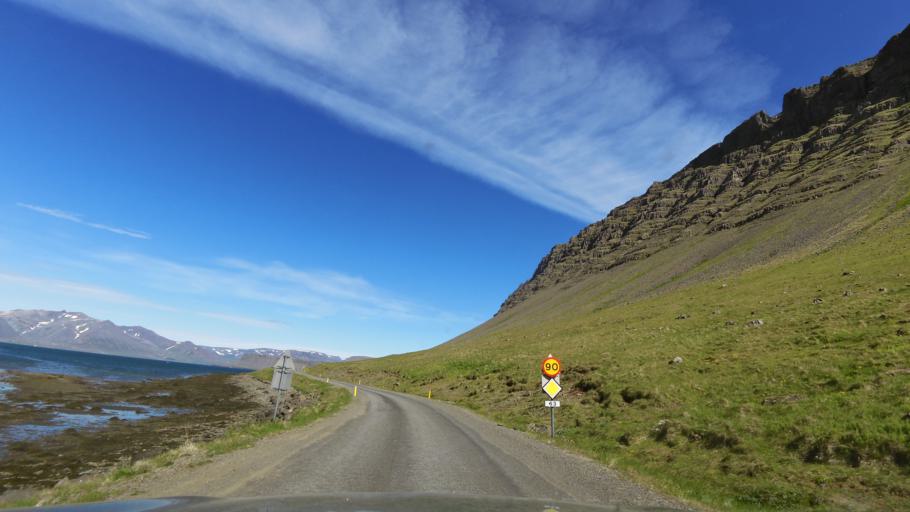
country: IS
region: Westfjords
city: Isafjoerdur
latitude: 65.6743
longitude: -23.6009
